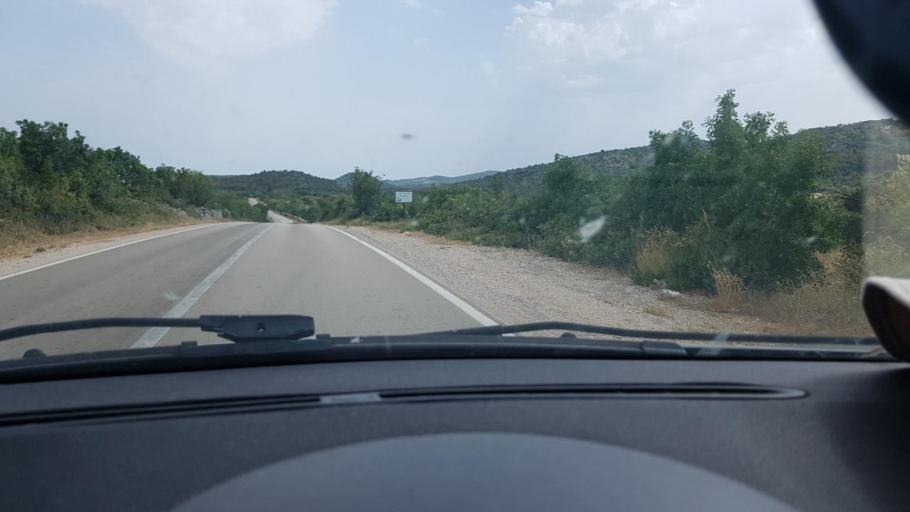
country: HR
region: Sibensko-Kniniska
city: Zaton
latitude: 43.8163
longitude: 15.7778
